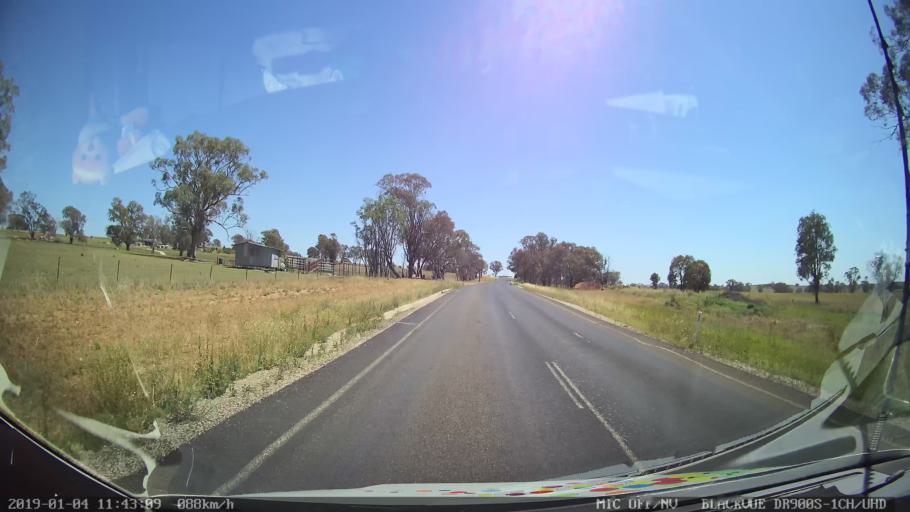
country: AU
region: New South Wales
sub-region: Cabonne
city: Molong
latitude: -32.9725
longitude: 148.7843
